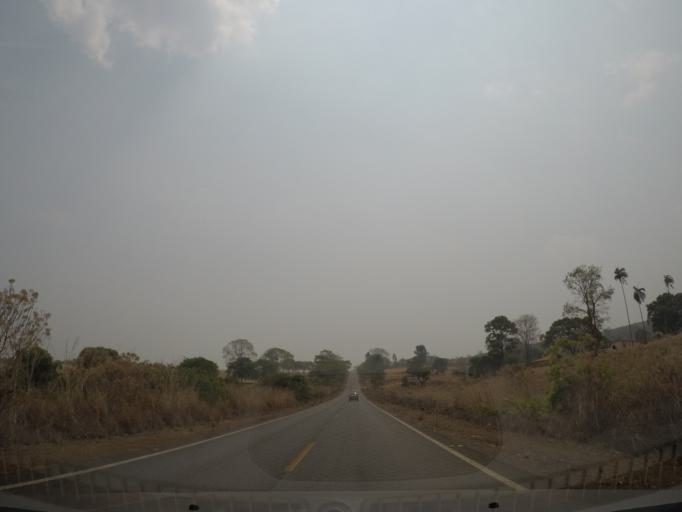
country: BR
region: Goias
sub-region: Pirenopolis
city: Pirenopolis
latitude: -15.8967
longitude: -48.8773
